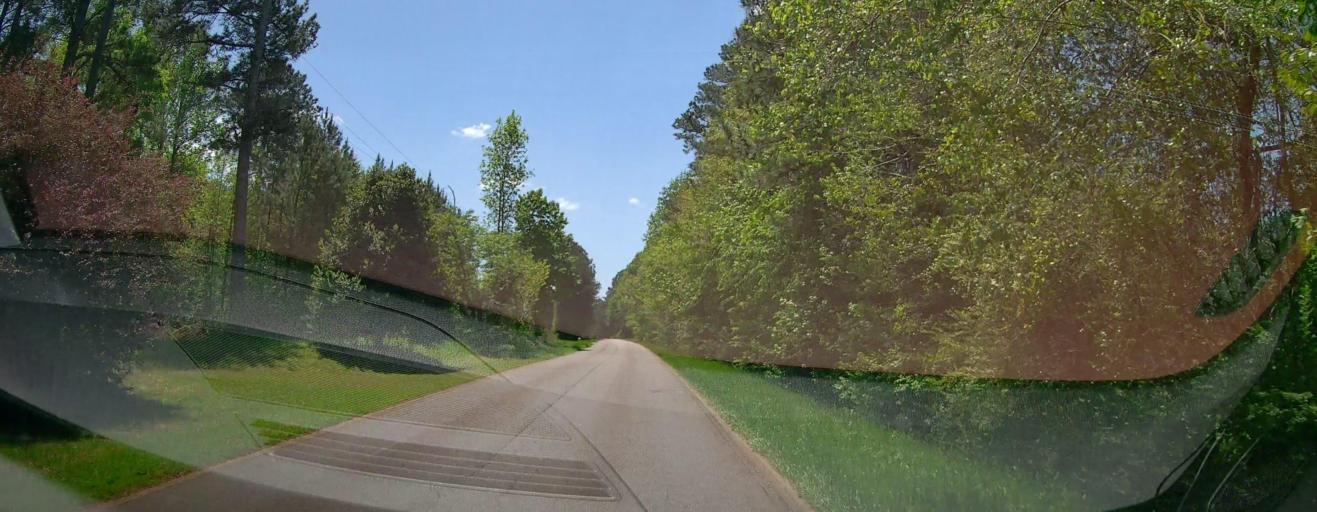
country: US
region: Georgia
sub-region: Jasper County
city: Monticello
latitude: 33.3254
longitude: -83.7079
